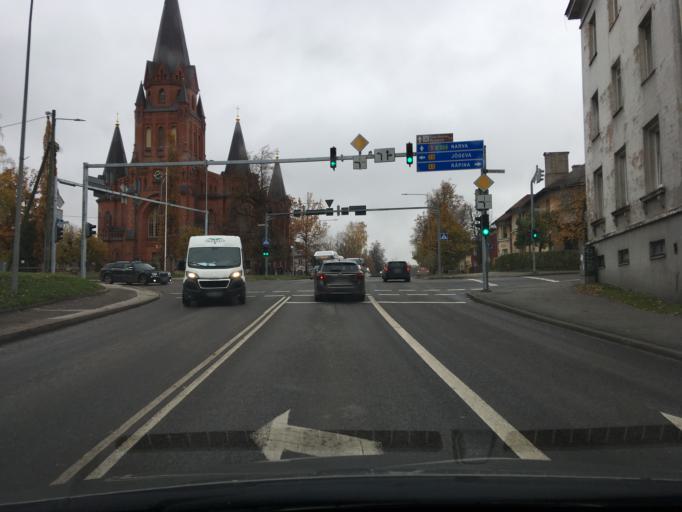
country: EE
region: Tartu
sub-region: Tartu linn
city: Tartu
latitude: 58.3893
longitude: 26.7282
